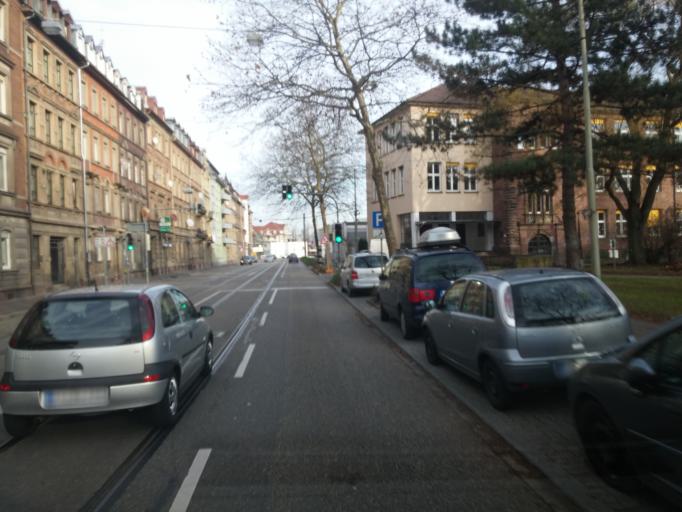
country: DE
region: Baden-Wuerttemberg
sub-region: Karlsruhe Region
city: Karlsruhe
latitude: 49.0075
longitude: 8.4145
